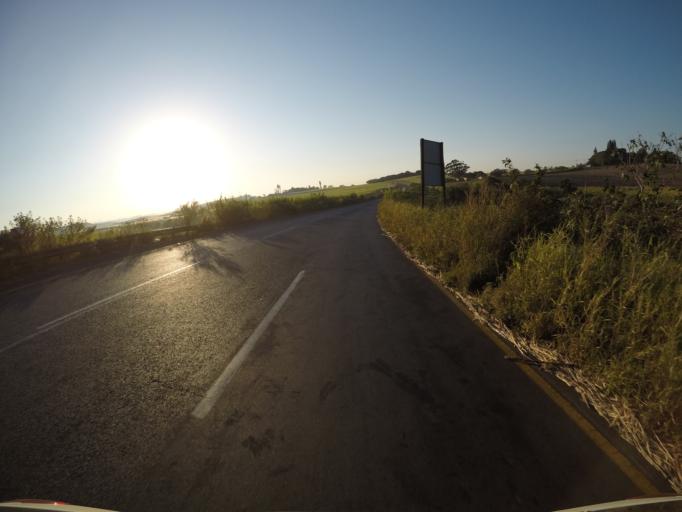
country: ZA
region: KwaZulu-Natal
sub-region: uThungulu District Municipality
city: eSikhawini
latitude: -28.9489
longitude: 31.6918
